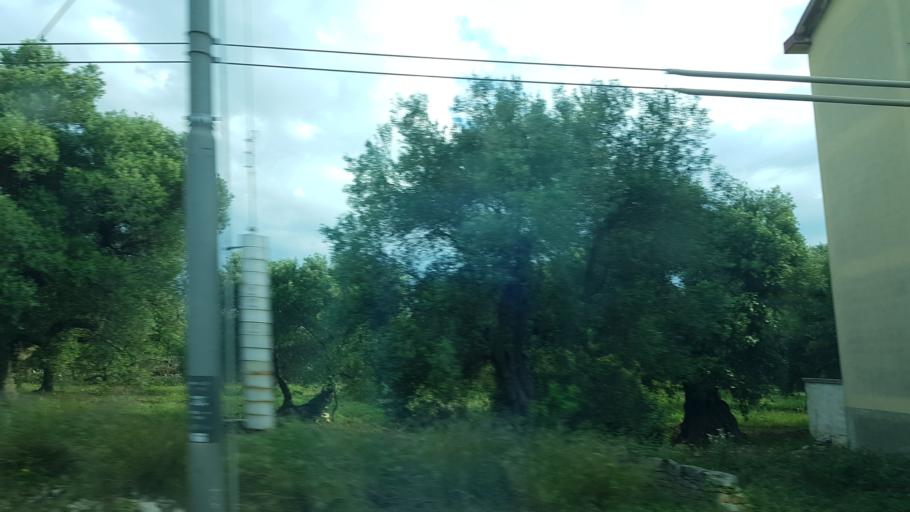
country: IT
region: Apulia
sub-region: Provincia di Brindisi
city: Ostuni
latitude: 40.7514
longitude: 17.5839
